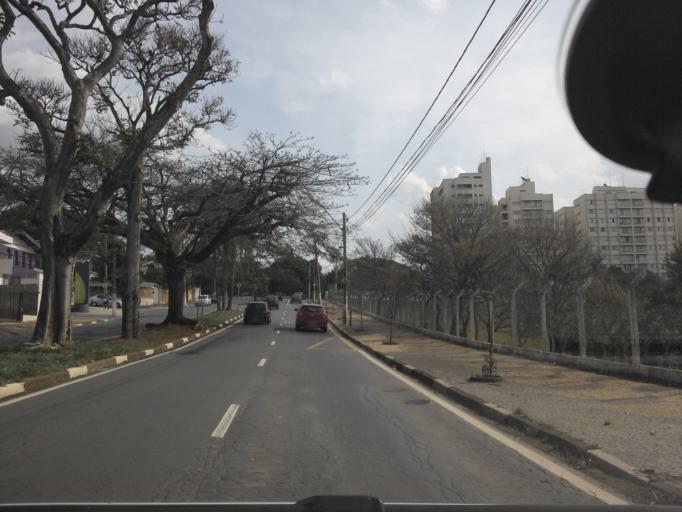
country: BR
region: Sao Paulo
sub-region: Campinas
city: Campinas
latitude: -22.8855
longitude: -47.0779
